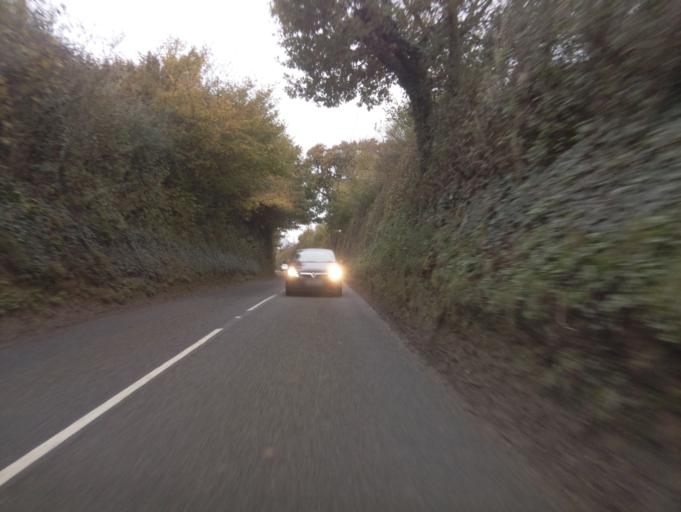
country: GB
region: England
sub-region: Dorset
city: Sherborne
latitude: 50.9617
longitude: -2.5454
